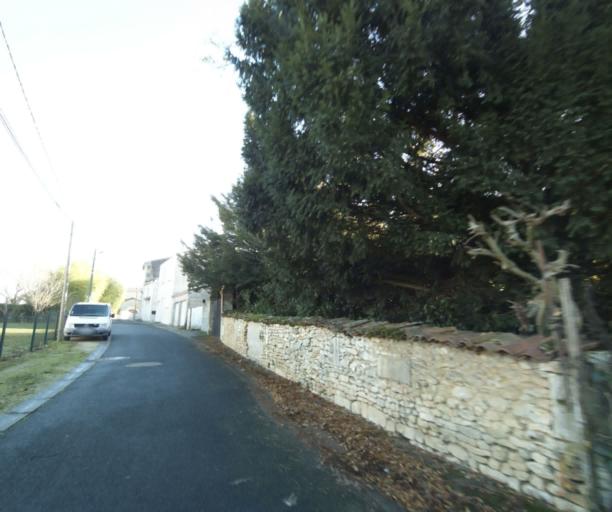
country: FR
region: Poitou-Charentes
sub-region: Departement de la Charente-Maritime
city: Burie
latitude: 45.7731
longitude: -0.4256
